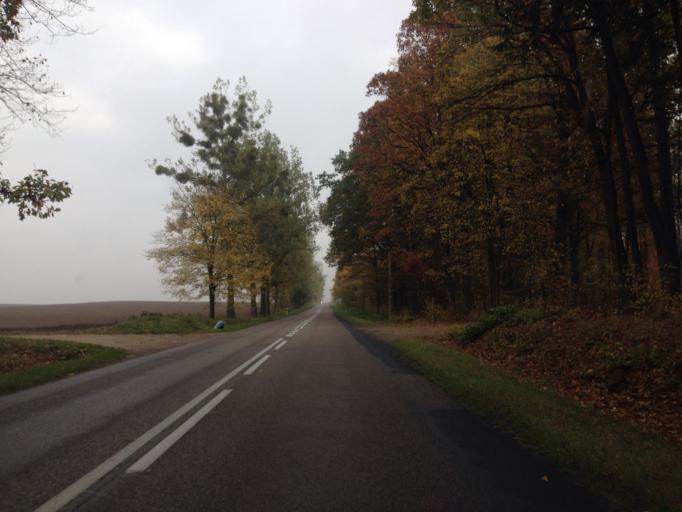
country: PL
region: Warmian-Masurian Voivodeship
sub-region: Powiat dzialdowski
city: Lidzbark
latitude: 53.2592
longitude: 19.7516
